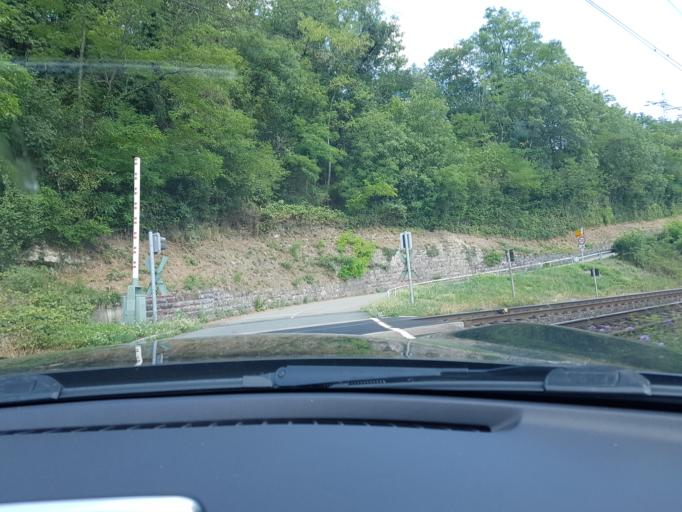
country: DE
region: Baden-Wuerttemberg
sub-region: Karlsruhe Region
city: Neckarzimmern
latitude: 49.3183
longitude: 9.1348
